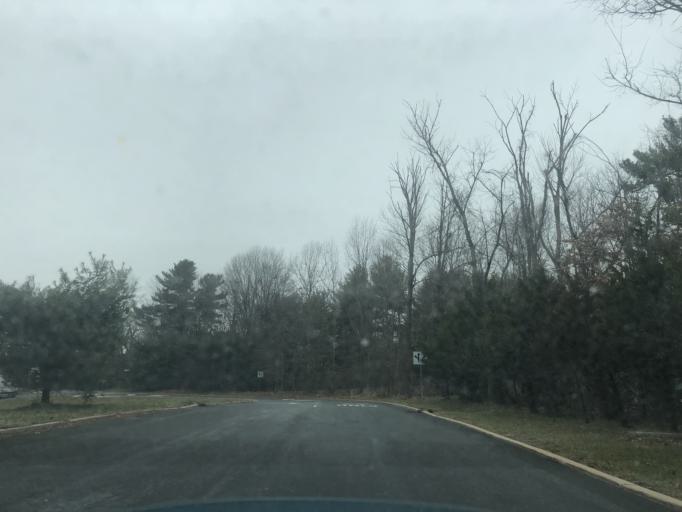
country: US
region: New Jersey
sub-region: Somerset County
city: Kingston
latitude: 40.3497
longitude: -74.6169
